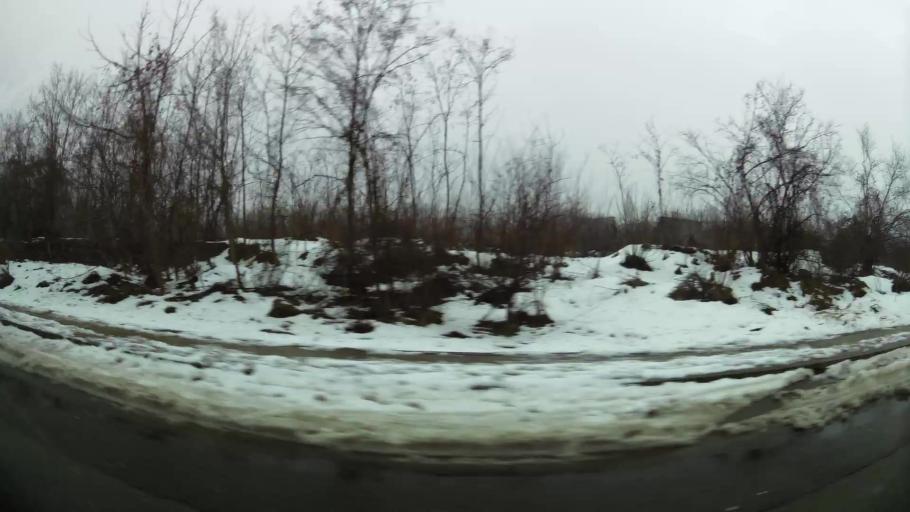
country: RS
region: Central Serbia
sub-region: Belgrade
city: Vozdovac
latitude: 44.7588
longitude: 20.4825
